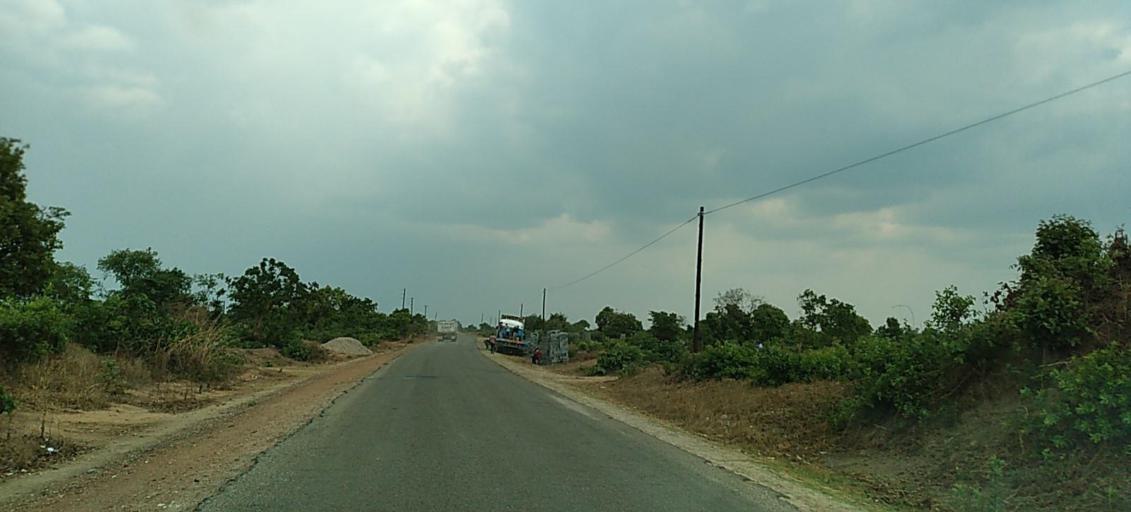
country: ZM
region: Copperbelt
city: Kalulushi
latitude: -12.8695
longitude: 28.1210
